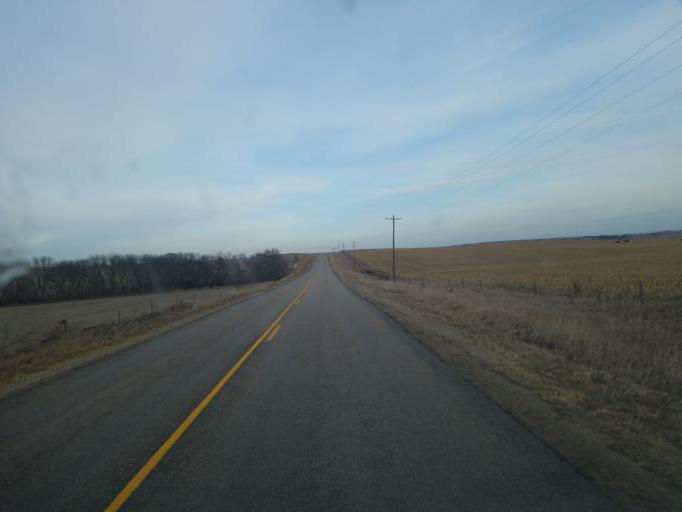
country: US
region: Nebraska
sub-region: Knox County
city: Creighton
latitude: 42.4662
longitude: -98.1498
